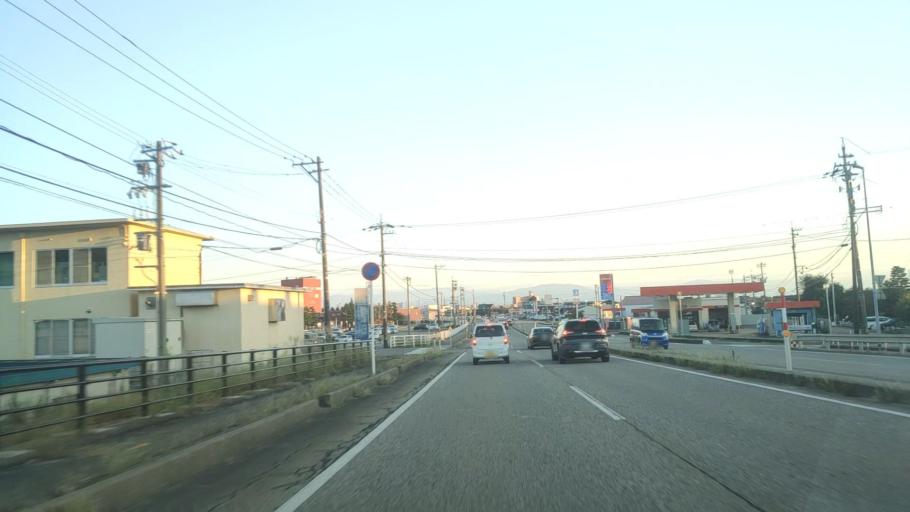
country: JP
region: Toyama
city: Takaoka
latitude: 36.7733
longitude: 137.0007
